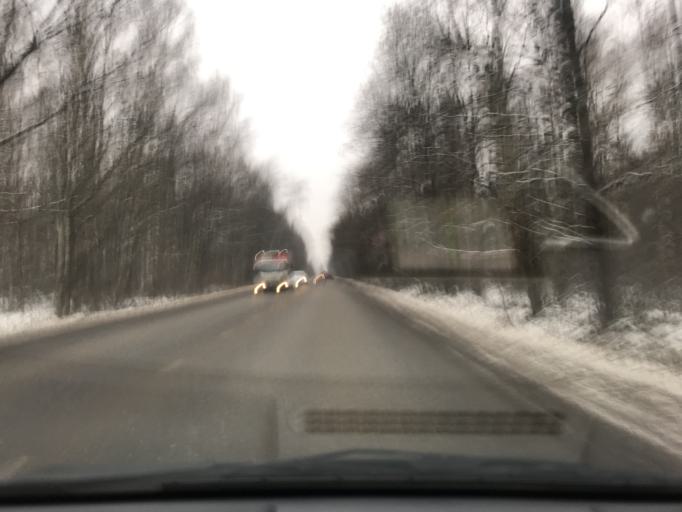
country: RU
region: Moskovskaya
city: Elektrostal'
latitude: 55.8165
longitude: 38.4565
